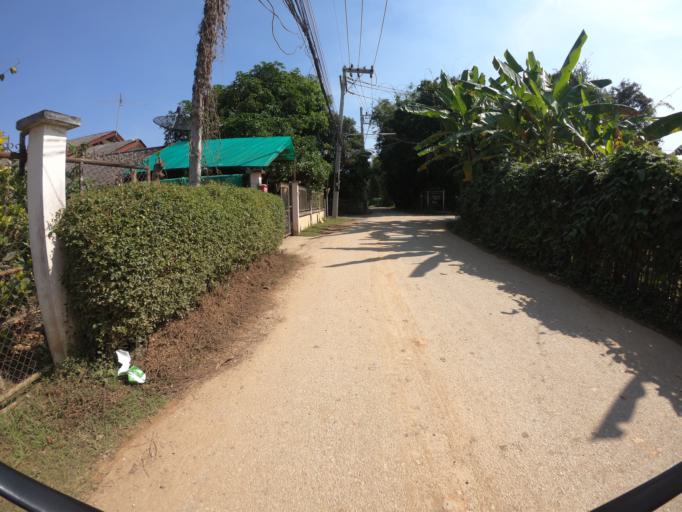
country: TH
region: Chiang Mai
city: San Sai
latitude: 18.8704
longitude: 98.9855
